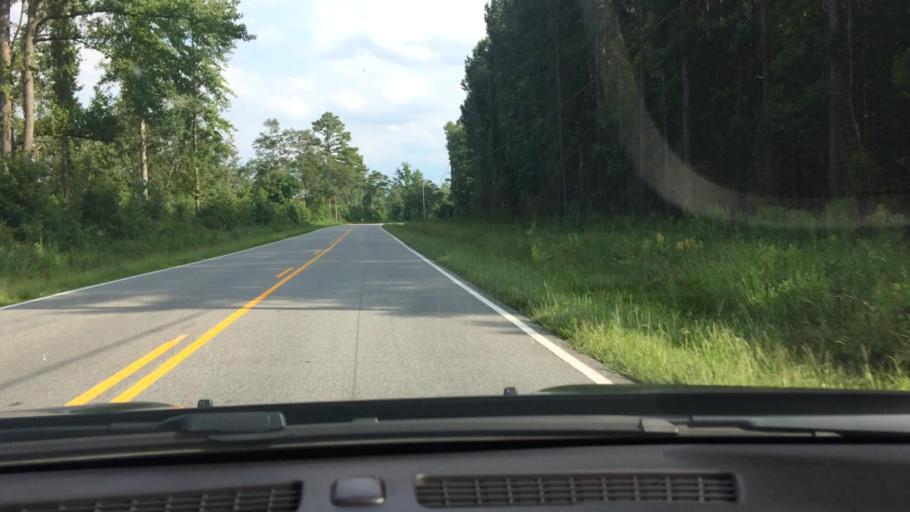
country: US
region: North Carolina
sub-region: Pitt County
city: Winterville
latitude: 35.5142
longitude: -77.3826
